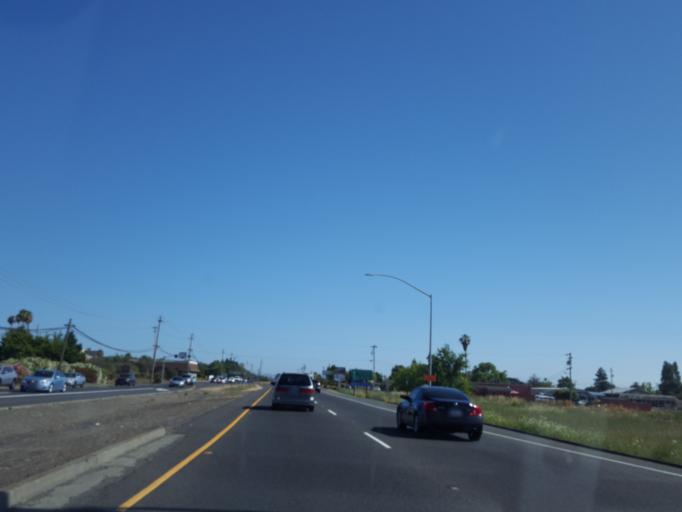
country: US
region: California
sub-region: Napa County
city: American Canyon
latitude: 38.1794
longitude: -122.2549
